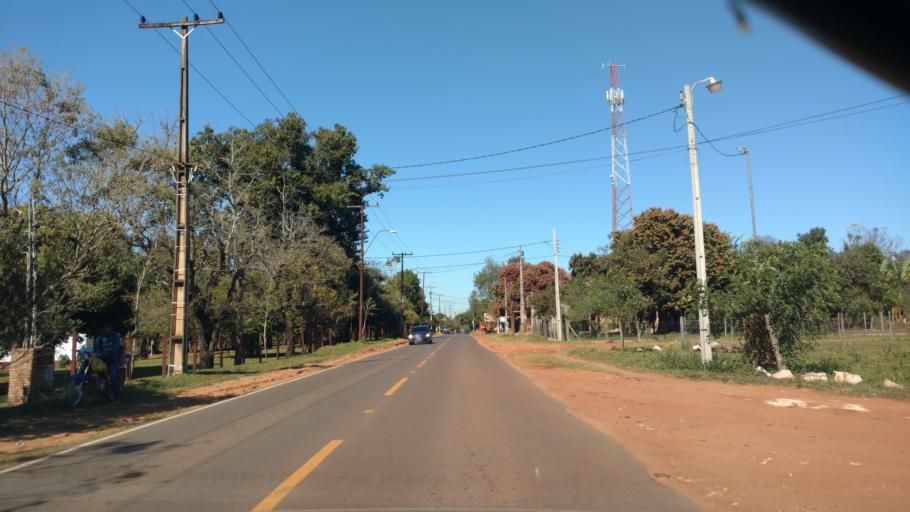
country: PY
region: Paraguari
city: Yaguaron
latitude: -25.5543
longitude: -57.2832
